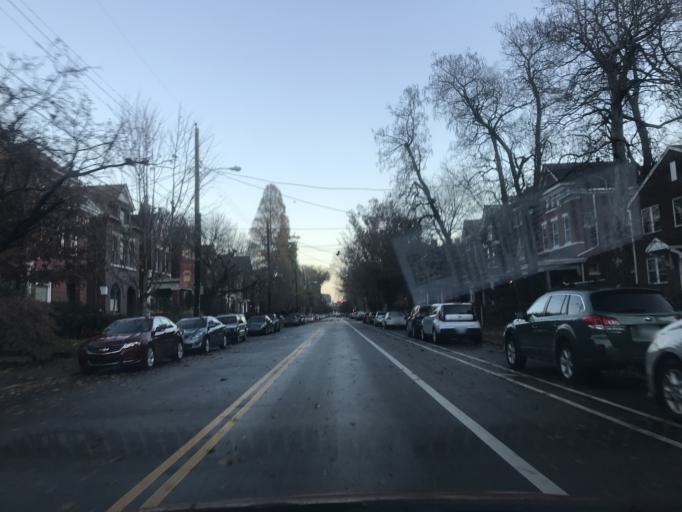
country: US
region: Kentucky
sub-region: Jefferson County
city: Louisville
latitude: 38.2326
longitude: -85.7540
